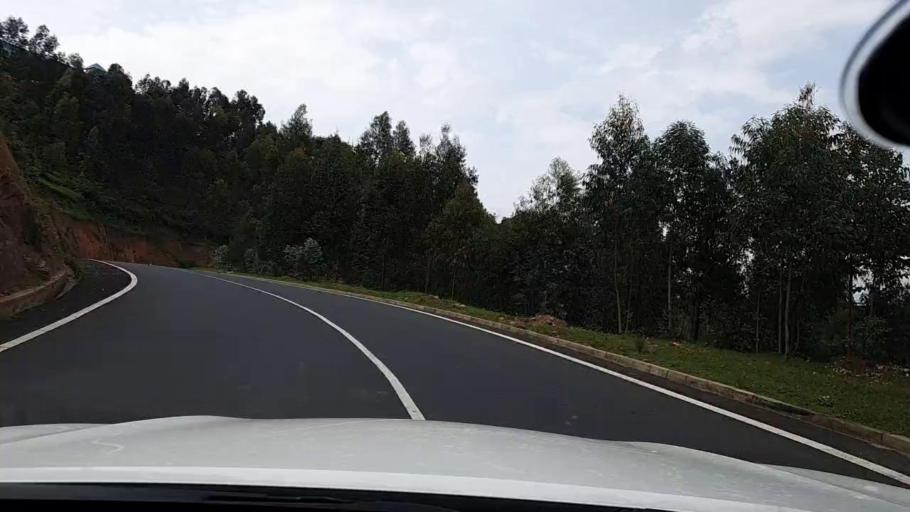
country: RW
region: Western Province
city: Kibuye
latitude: -2.1747
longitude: 29.2917
